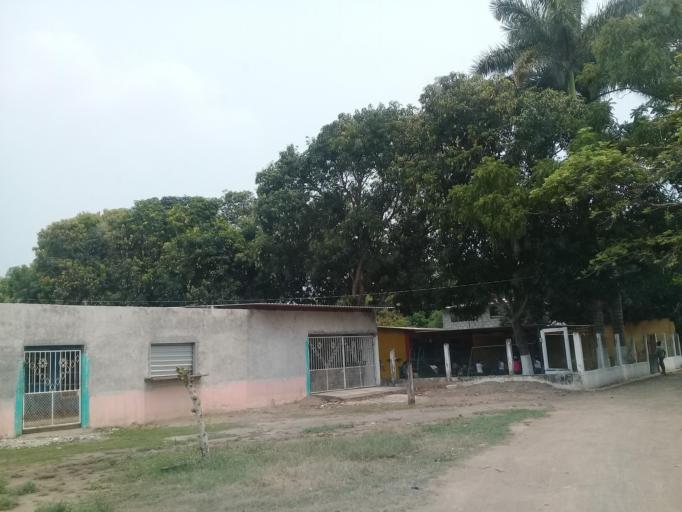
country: MX
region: Veracruz
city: Jamapa
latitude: 18.9511
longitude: -96.1998
